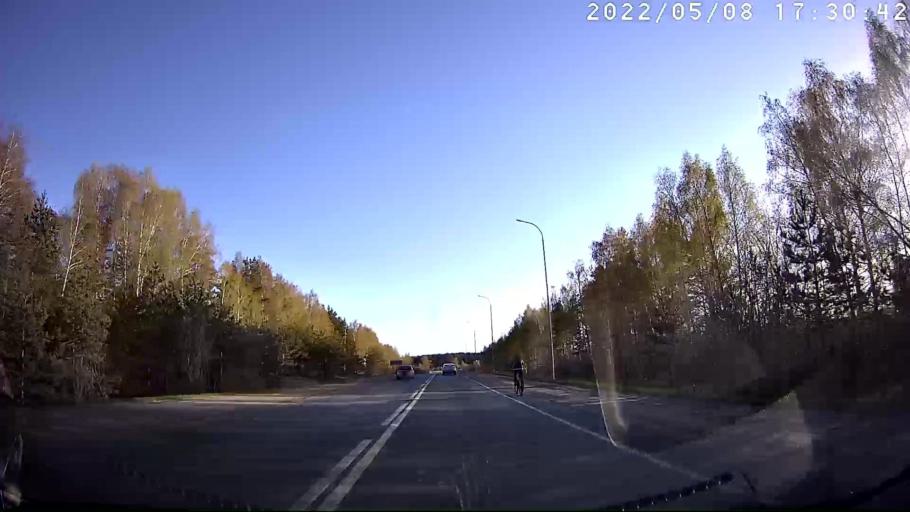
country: RU
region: Mariy-El
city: Volzhsk
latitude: 55.9071
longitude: 48.3604
